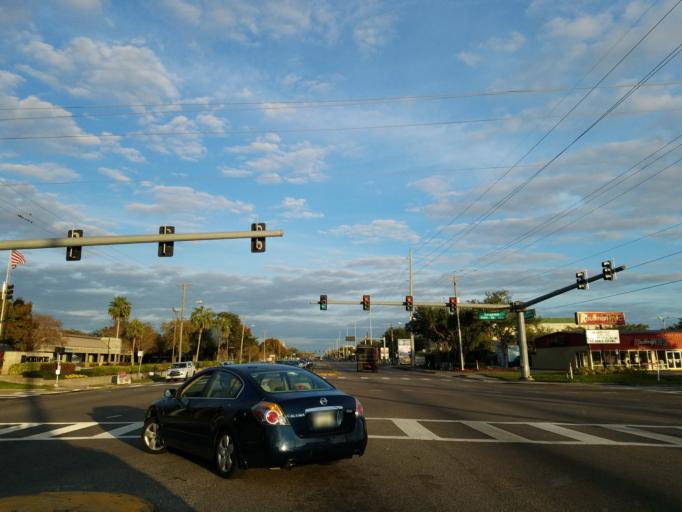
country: US
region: Florida
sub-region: Hillsborough County
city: Egypt Lake-Leto
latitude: 28.0256
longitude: -82.5421
